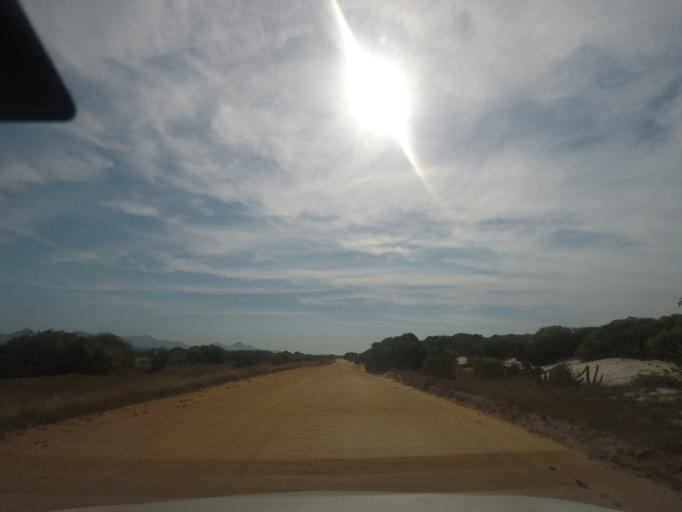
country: BR
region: Rio de Janeiro
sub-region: Marica
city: Marica
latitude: -22.9599
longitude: -42.8672
